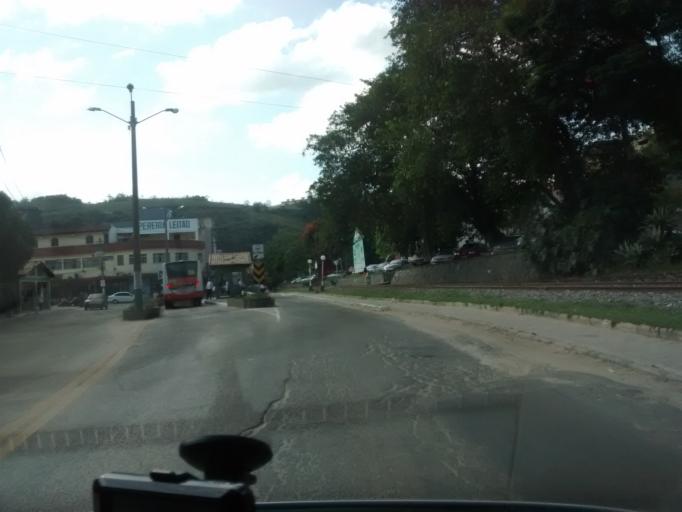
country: BR
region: Rio de Janeiro
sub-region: Miguel Pereira
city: Miguel Pereira
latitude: -22.4570
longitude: -43.4712
